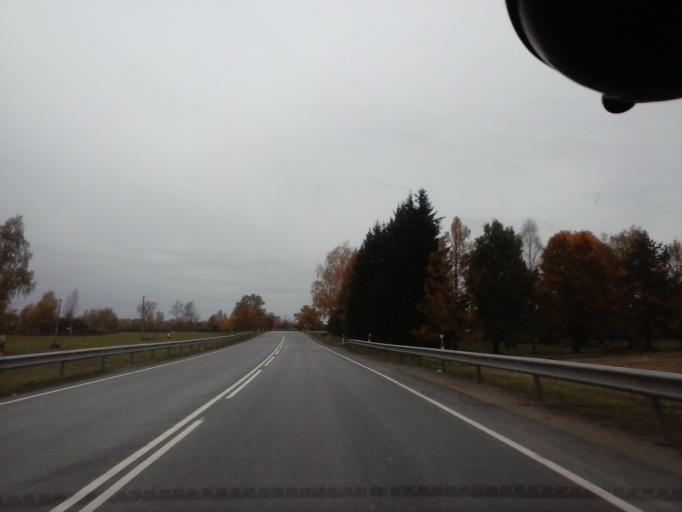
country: EE
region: Tartu
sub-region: Puhja vald
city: Puhja
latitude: 58.5550
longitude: 26.2982
